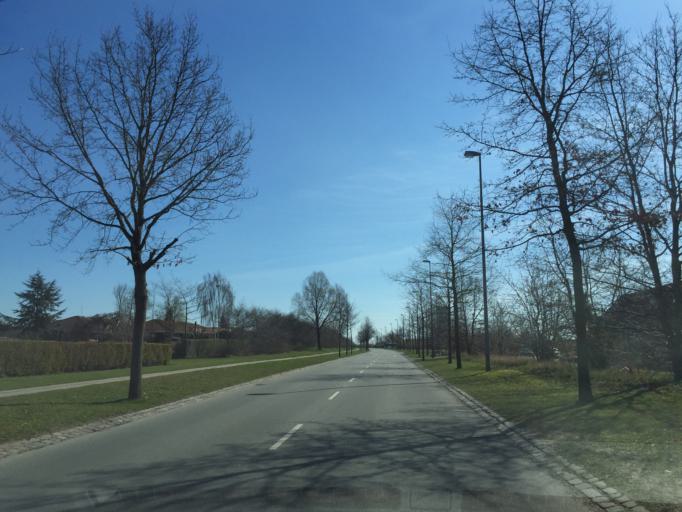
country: DK
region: South Denmark
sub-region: Odense Kommune
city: Neder Holluf
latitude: 55.3697
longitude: 10.4629
